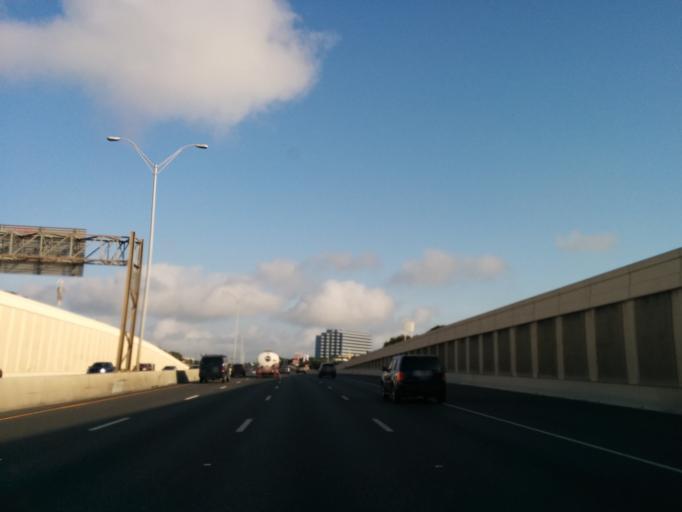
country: US
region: Texas
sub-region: Bexar County
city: Shavano Park
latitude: 29.5400
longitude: -98.5714
